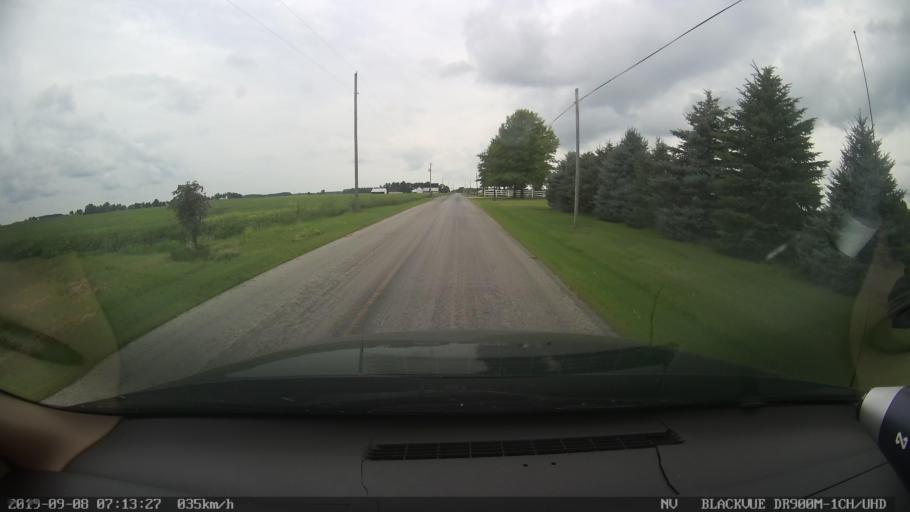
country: US
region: Ohio
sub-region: Richland County
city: Shelby
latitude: 40.9087
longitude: -82.6926
